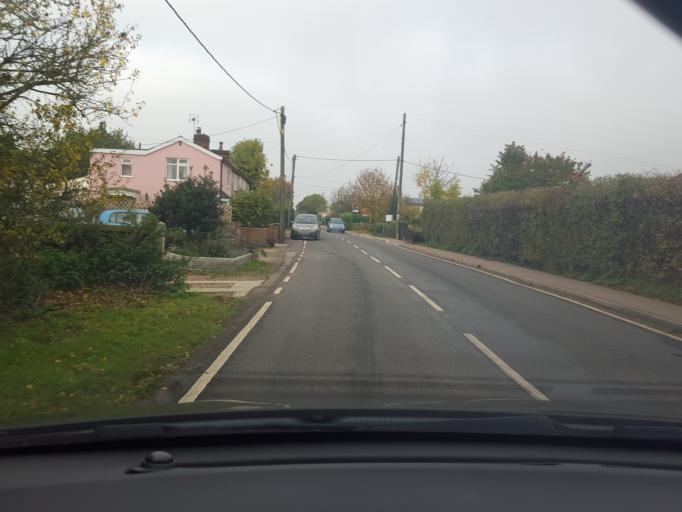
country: GB
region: England
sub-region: Essex
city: Alresford
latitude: 51.9077
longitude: 1.0052
